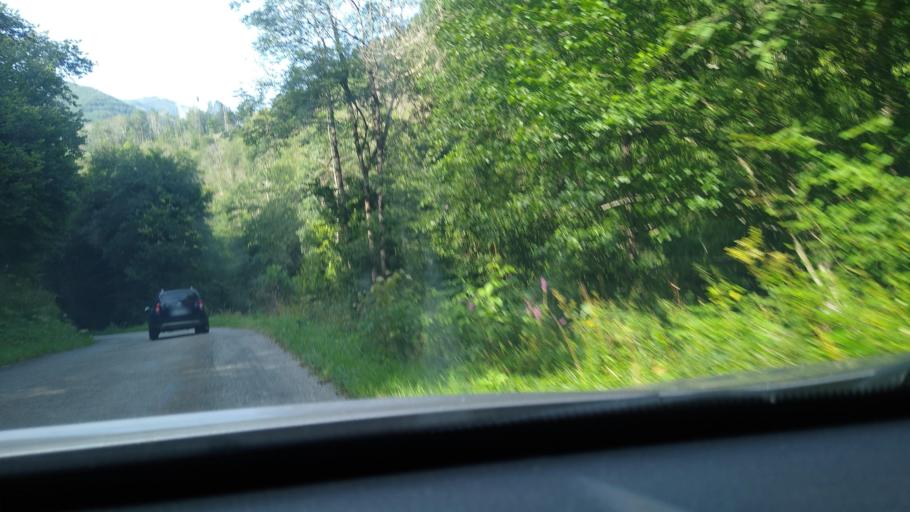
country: FR
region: Midi-Pyrenees
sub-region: Departement de l'Ariege
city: Saint-Girons
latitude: 42.7974
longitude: 1.1911
